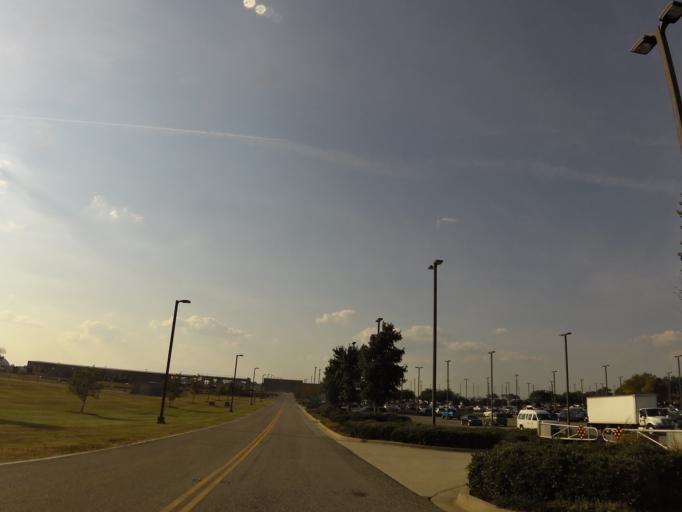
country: US
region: Tennessee
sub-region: Blount County
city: Alcoa
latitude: 35.8021
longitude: -83.9917
